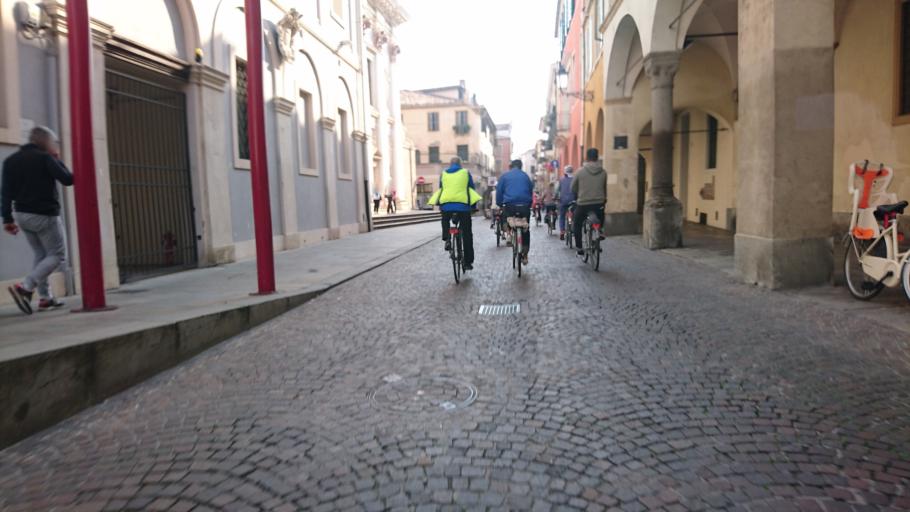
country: IT
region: Veneto
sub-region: Provincia di Padova
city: Padova
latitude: 45.4083
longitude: 11.8815
